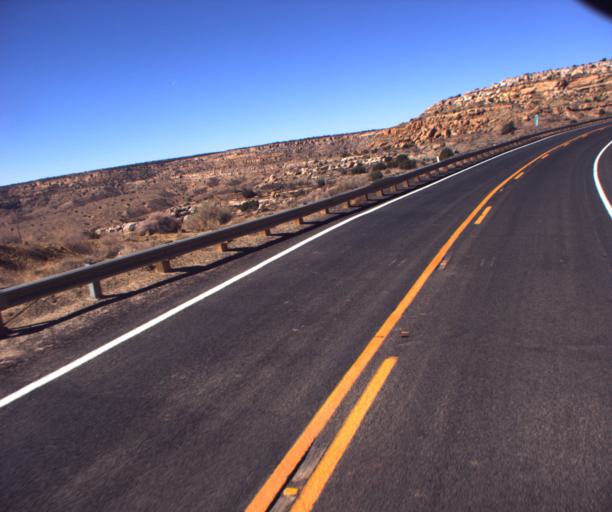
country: US
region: Arizona
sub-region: Navajo County
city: First Mesa
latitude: 35.8955
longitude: -110.6632
